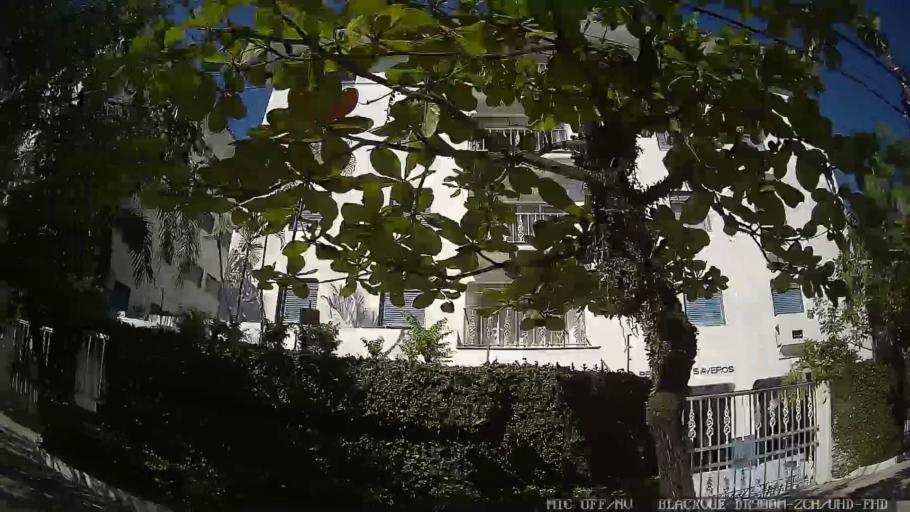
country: BR
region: Sao Paulo
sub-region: Guaruja
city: Guaruja
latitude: -23.9923
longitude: -46.2407
